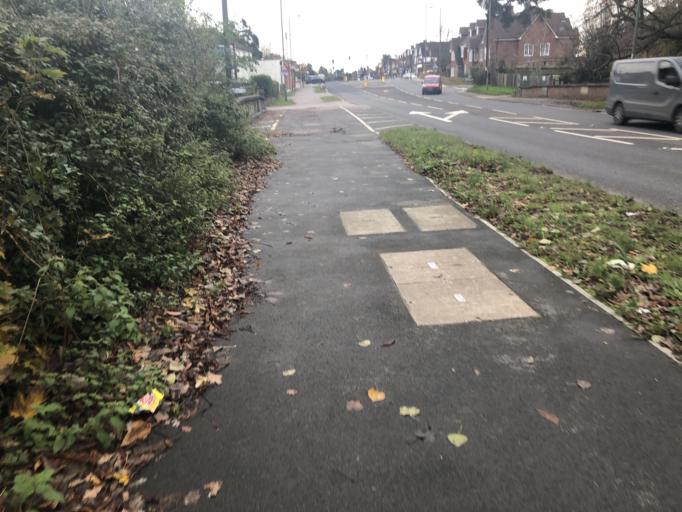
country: GB
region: England
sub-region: Surrey
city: Salfords
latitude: 51.2052
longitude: -0.1675
